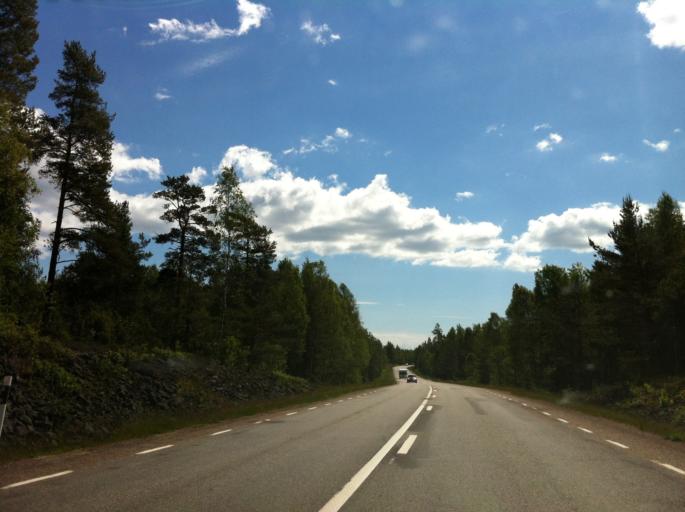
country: SE
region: Vaestra Goetaland
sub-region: Amals Kommun
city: Amal
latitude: 59.0271
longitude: 12.6738
